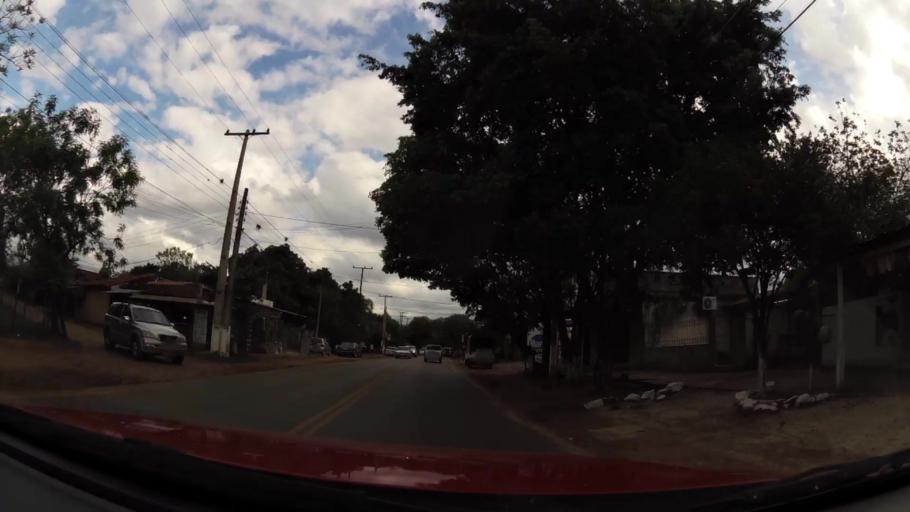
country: PY
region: Central
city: San Lorenzo
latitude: -25.2764
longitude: -57.4858
